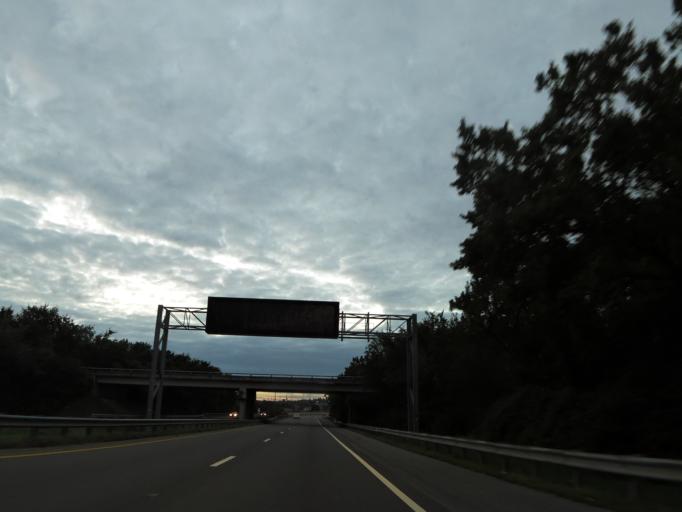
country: US
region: Tennessee
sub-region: Davidson County
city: Belle Meade
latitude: 36.1631
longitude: -86.8678
